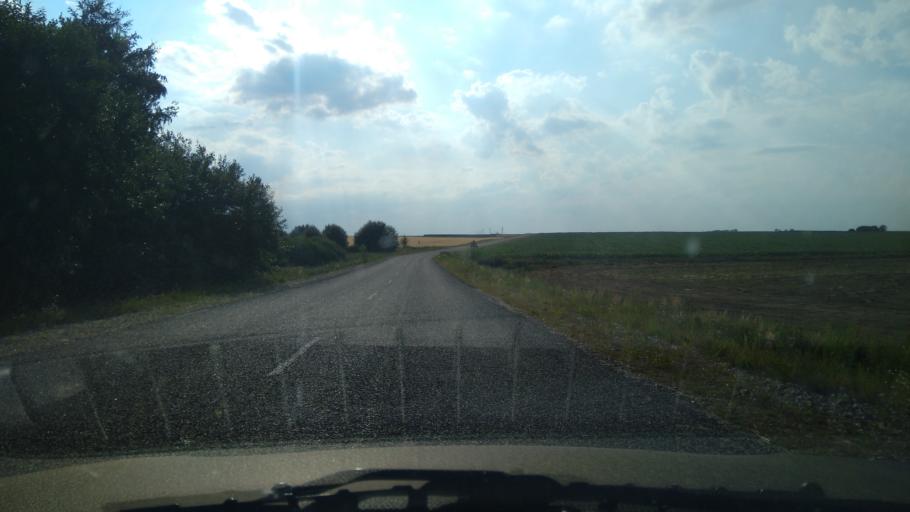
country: BY
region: Brest
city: Lyakhavichy
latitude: 53.0302
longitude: 26.3179
